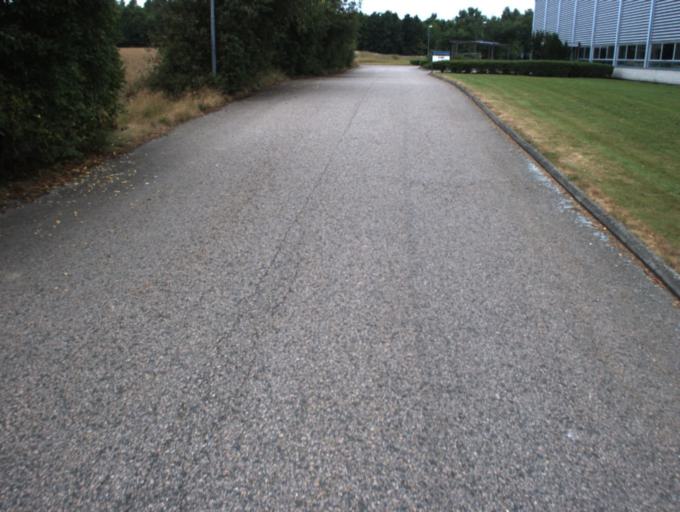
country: SE
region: Skane
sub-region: Helsingborg
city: Odakra
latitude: 56.0815
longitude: 12.7464
